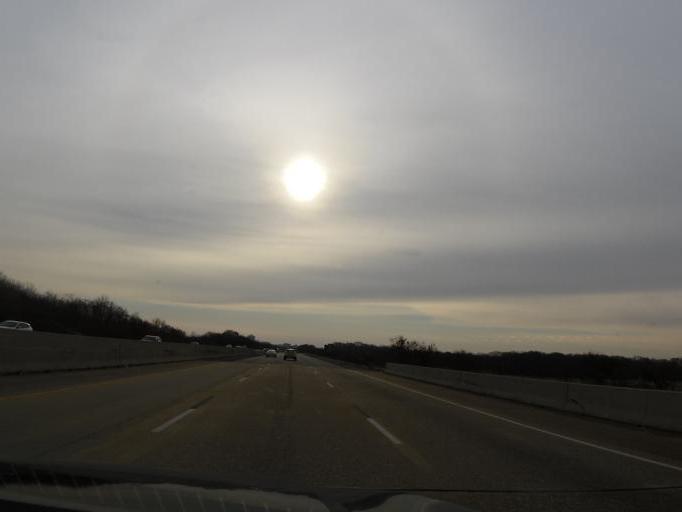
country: US
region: Alabama
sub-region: Montgomery County
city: Montgomery
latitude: 32.4045
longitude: -86.3412
